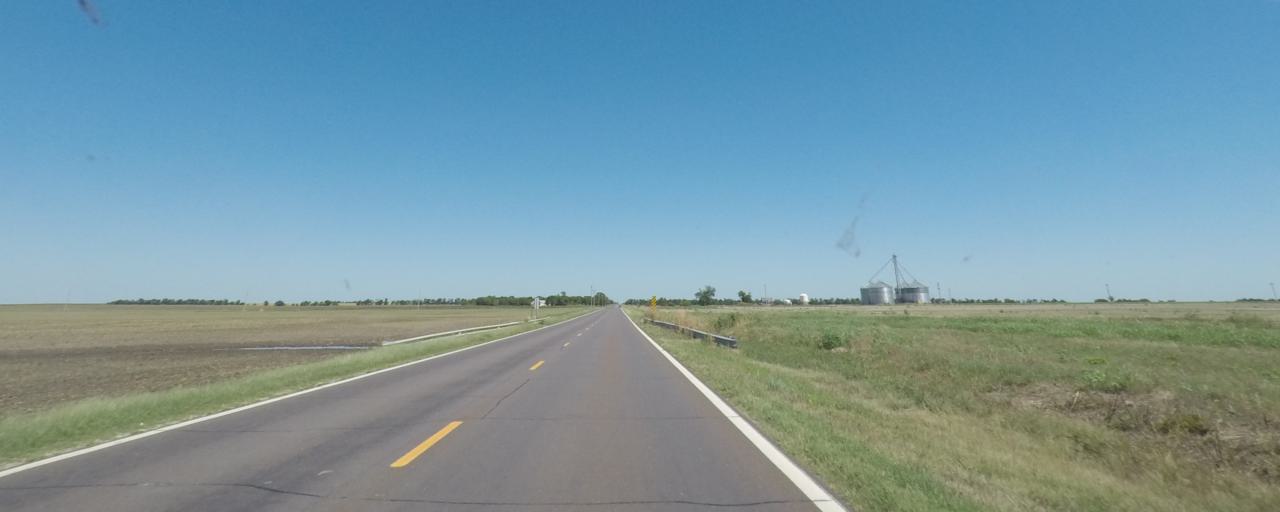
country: US
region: Kansas
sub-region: Sumner County
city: Wellington
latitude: 37.1849
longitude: -97.4021
